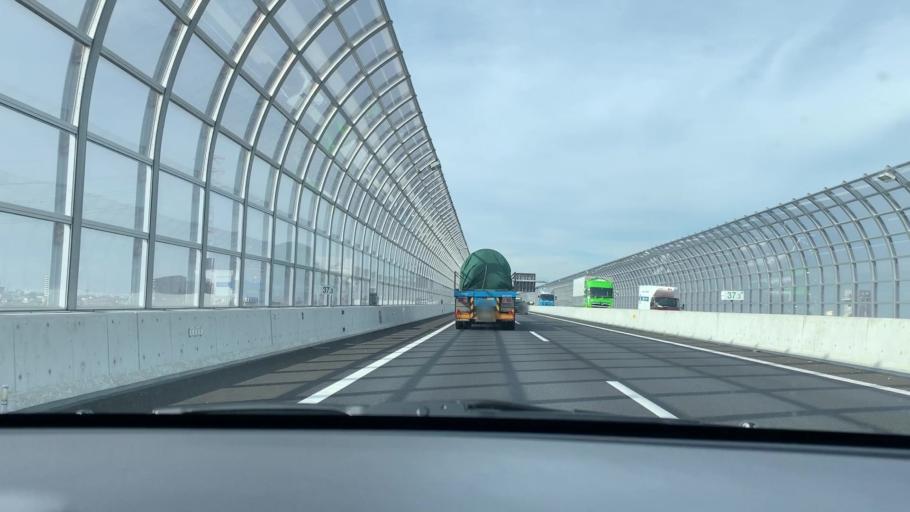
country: JP
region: Chiba
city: Matsudo
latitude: 35.7724
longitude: 139.8918
